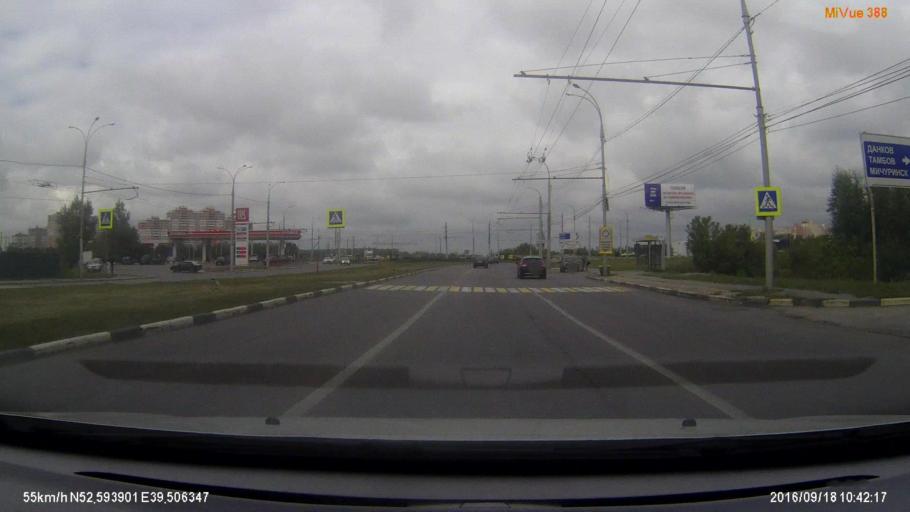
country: RU
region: Lipetsk
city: Syrskoye
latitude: 52.5937
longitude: 39.5067
